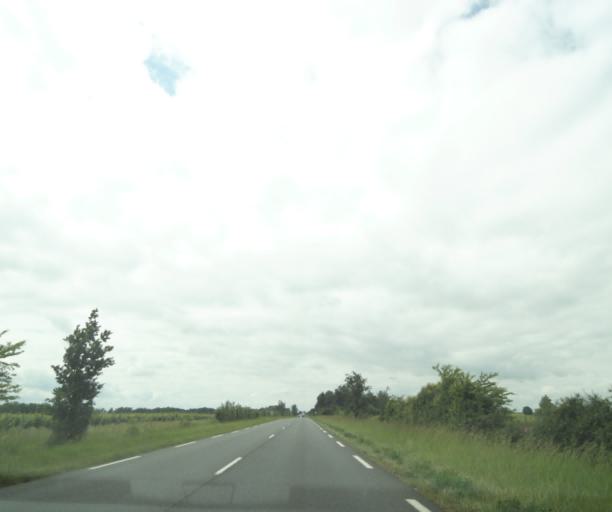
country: FR
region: Pays de la Loire
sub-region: Departement de Maine-et-Loire
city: Montreuil-Bellay
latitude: 47.1561
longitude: -0.1463
